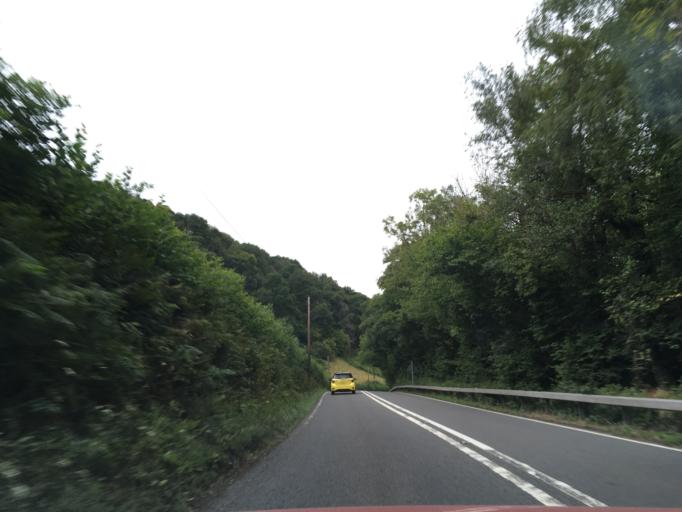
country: GB
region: Wales
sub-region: Carmarthenshire
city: Llandovery
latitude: 51.9821
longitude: -3.7072
